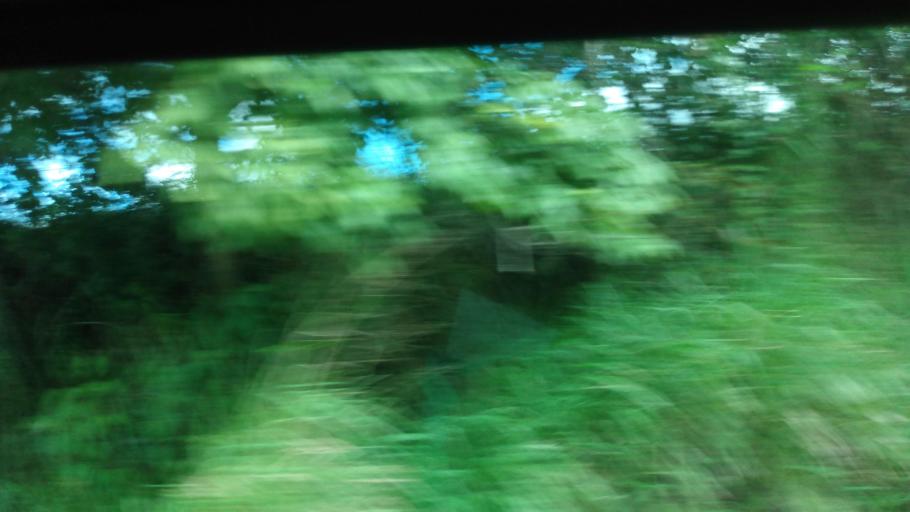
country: BR
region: Pernambuco
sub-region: Quipapa
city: Quipapa
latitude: -8.7766
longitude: -35.9427
